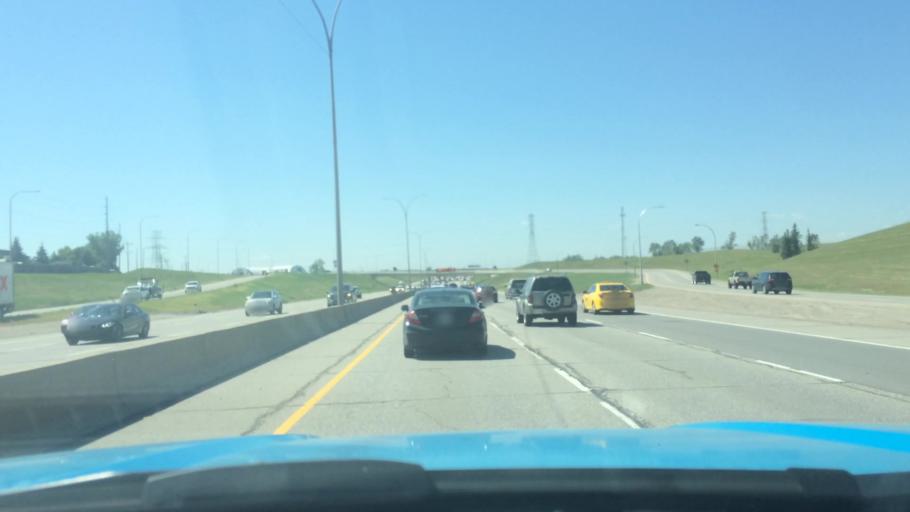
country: CA
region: Alberta
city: Calgary
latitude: 51.0208
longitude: -114.0022
